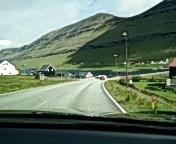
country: FO
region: Nordoyar
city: Klaksvik
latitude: 62.2973
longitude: -6.5280
